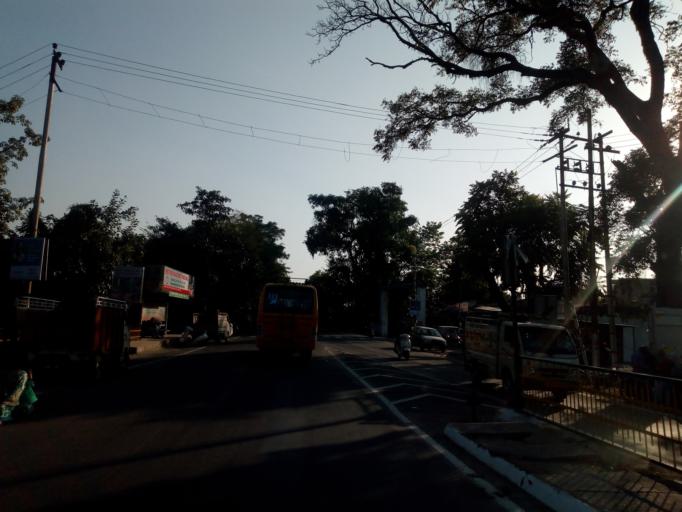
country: IN
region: Uttarakhand
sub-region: Dehradun
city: Dehradun
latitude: 30.3474
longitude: 78.0461
